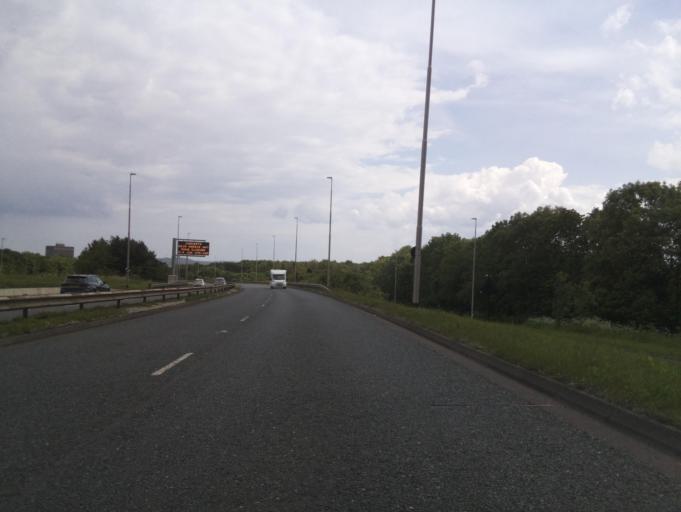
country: GB
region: England
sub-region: Sunderland
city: Washington
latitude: 54.9010
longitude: -1.5540
